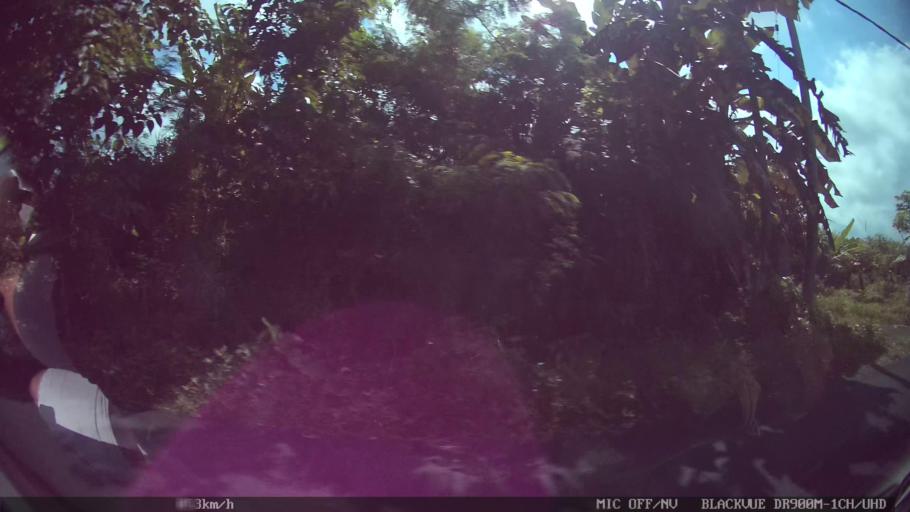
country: ID
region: Bali
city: Banjar Kelodan
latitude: -8.5243
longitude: 115.3287
